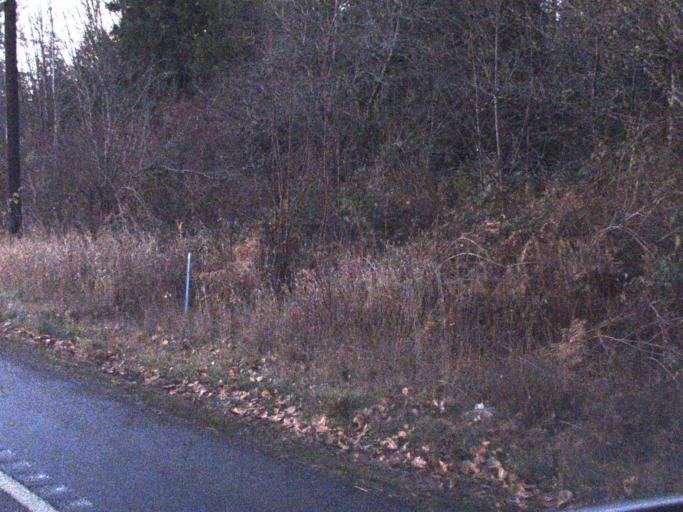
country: US
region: Washington
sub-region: Skagit County
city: Sedro-Woolley
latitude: 48.5282
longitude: -121.9153
